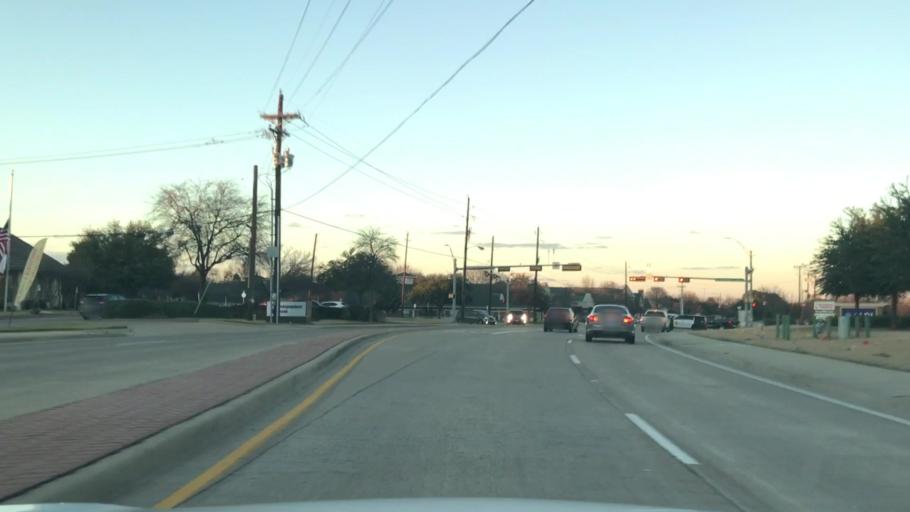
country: US
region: Texas
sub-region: Rockwall County
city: Rockwall
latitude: 32.8860
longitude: -96.4739
